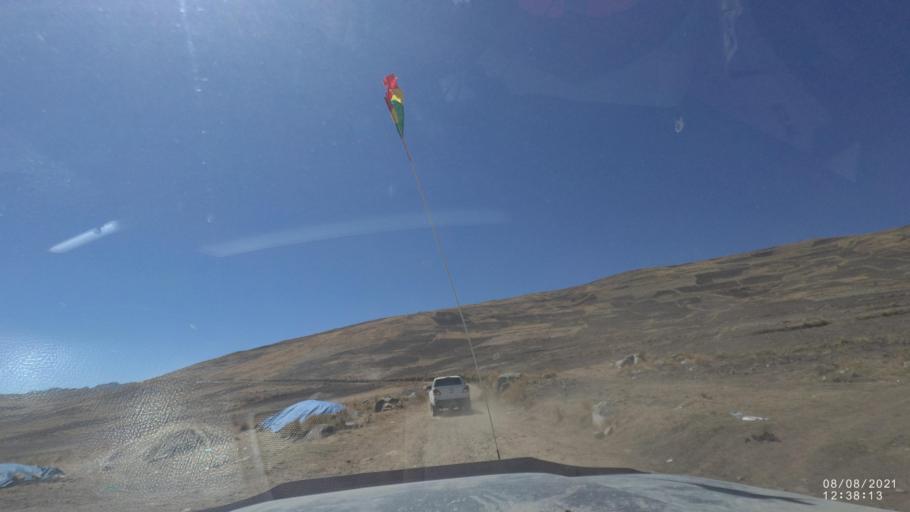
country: BO
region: Cochabamba
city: Colchani
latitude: -16.8340
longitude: -66.6258
